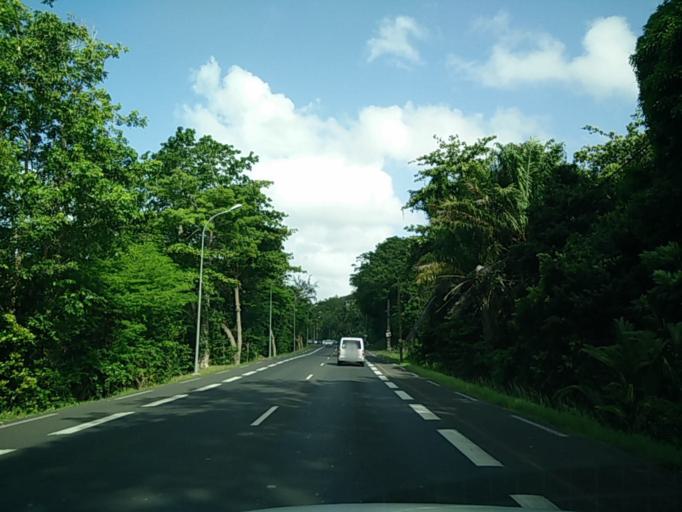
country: GP
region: Guadeloupe
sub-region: Guadeloupe
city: Le Gosier
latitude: 16.2176
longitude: -61.4850
